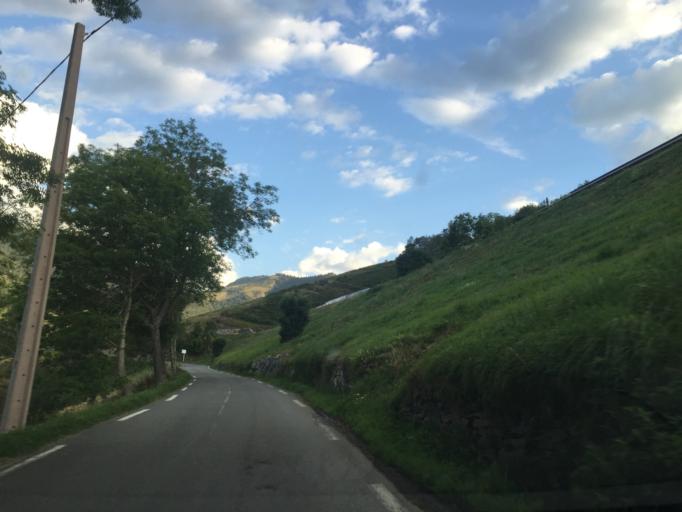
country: FR
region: Midi-Pyrenees
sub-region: Departement des Hautes-Pyrenees
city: Saint-Lary-Soulan
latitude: 42.9218
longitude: 0.3529
